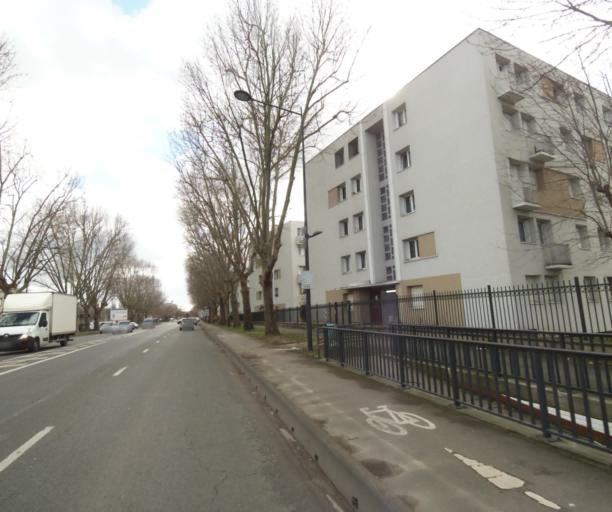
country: FR
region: Ile-de-France
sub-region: Departement de Seine-Saint-Denis
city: Saint-Denis
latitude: 48.9413
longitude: 2.3664
